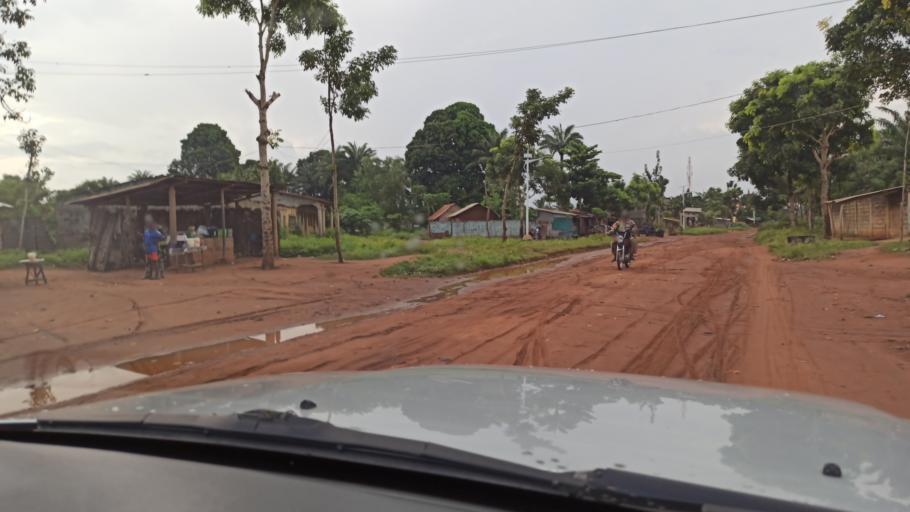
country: BJ
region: Queme
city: Porto-Novo
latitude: 6.4871
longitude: 2.6680
